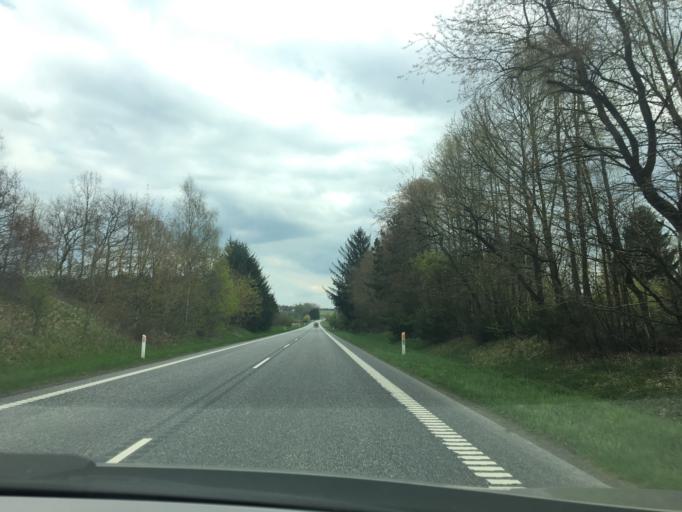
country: DK
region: Central Jutland
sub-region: Horsens Kommune
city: Braedstrup
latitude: 55.9403
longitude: 9.6525
